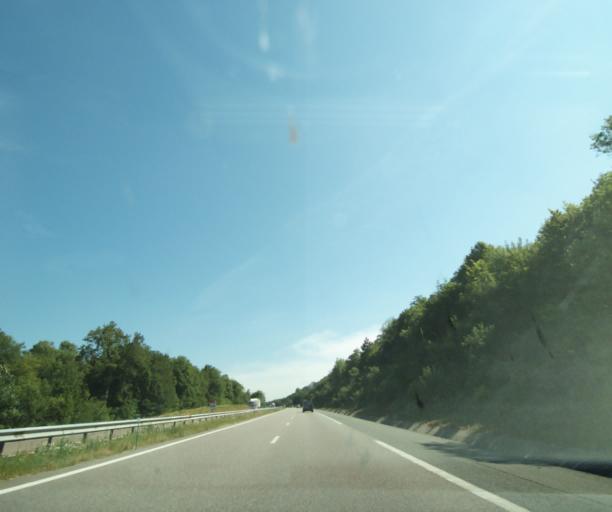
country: FR
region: Lorraine
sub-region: Departement de Meurthe-et-Moselle
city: Colombey-les-Belles
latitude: 48.4871
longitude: 5.9015
